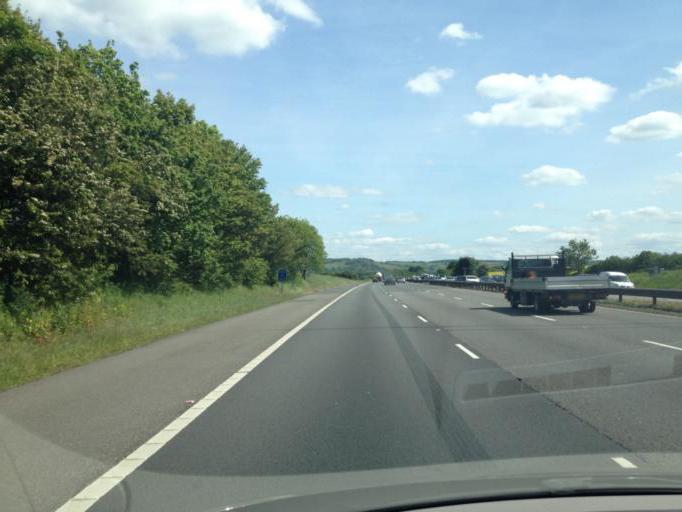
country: GB
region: England
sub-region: Oxfordshire
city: Thame
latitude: 51.6960
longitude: -0.9859
